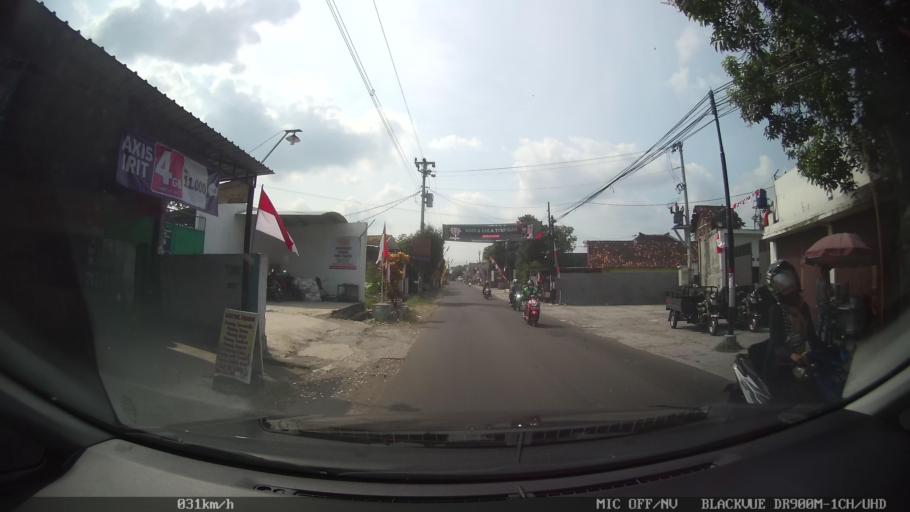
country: ID
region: Daerah Istimewa Yogyakarta
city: Depok
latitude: -7.7859
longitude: 110.4476
